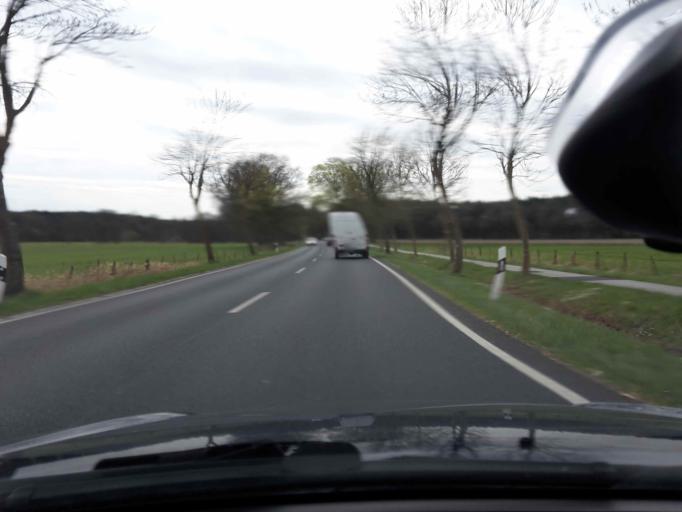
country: DE
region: Lower Saxony
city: Jesteburg
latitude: 53.2975
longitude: 9.9295
